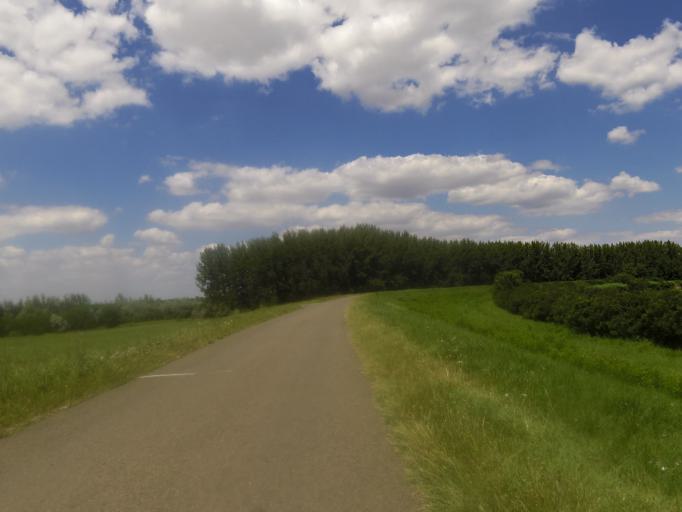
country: HU
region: Heves
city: Tiszanana
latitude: 47.5699
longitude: 20.6060
